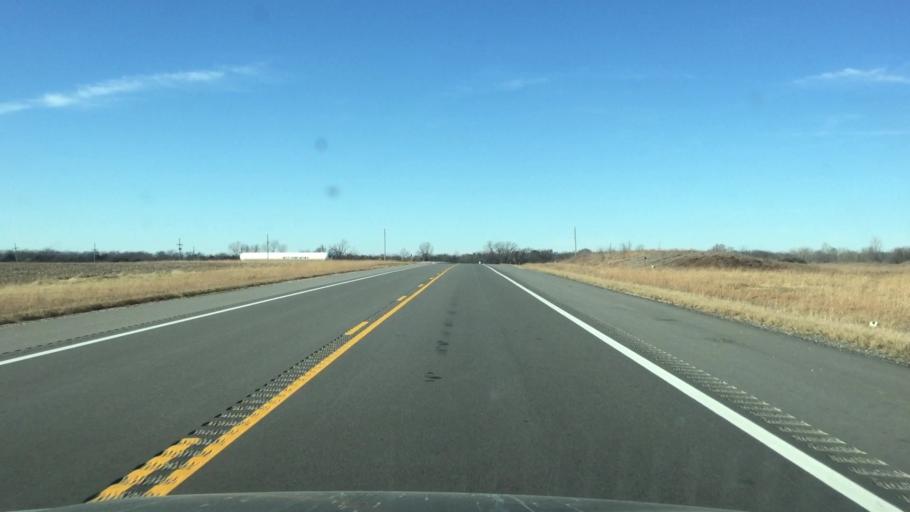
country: US
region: Kansas
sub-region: Franklin County
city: Ottawa
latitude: 38.4694
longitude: -95.2623
